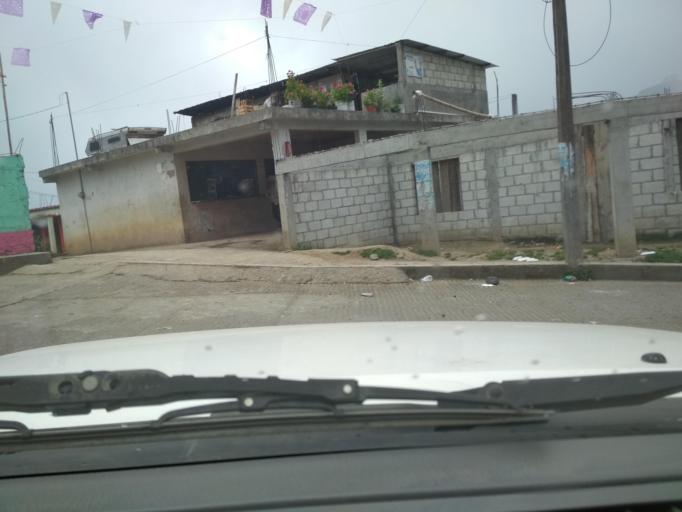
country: MX
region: Veracruz
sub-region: La Perla
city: Metlac Hernandez (Metlac Primero)
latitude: 18.9728
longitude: -97.1495
